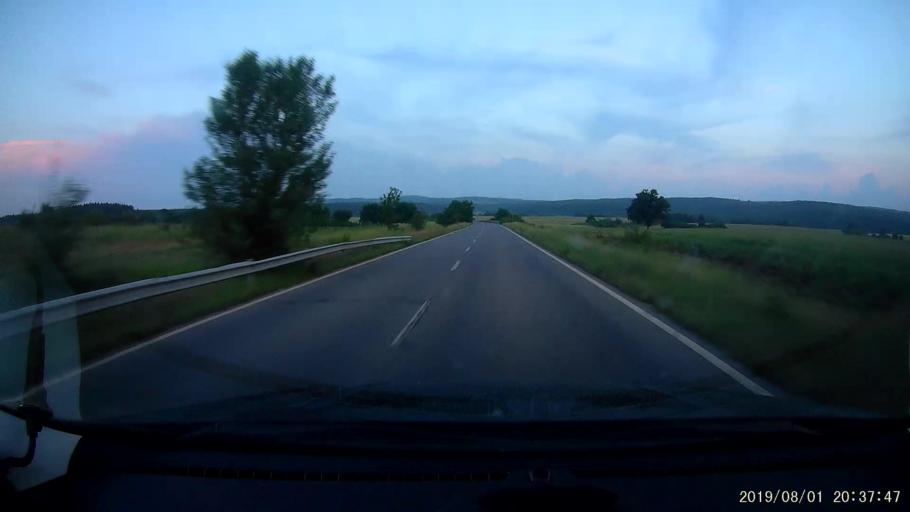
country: BG
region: Yambol
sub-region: Obshtina Elkhovo
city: Elkhovo
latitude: 42.0405
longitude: 26.5957
